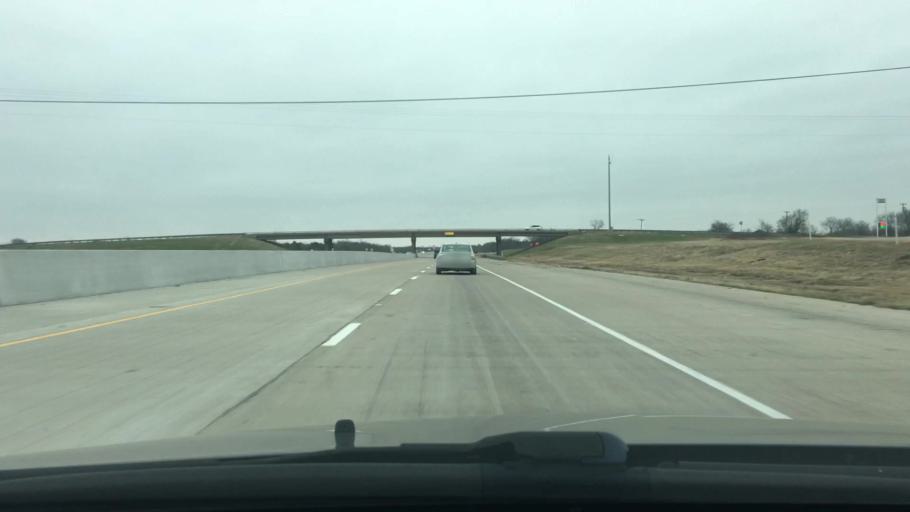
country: US
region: Texas
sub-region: Freestone County
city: Wortham
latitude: 31.8803
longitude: -96.3460
